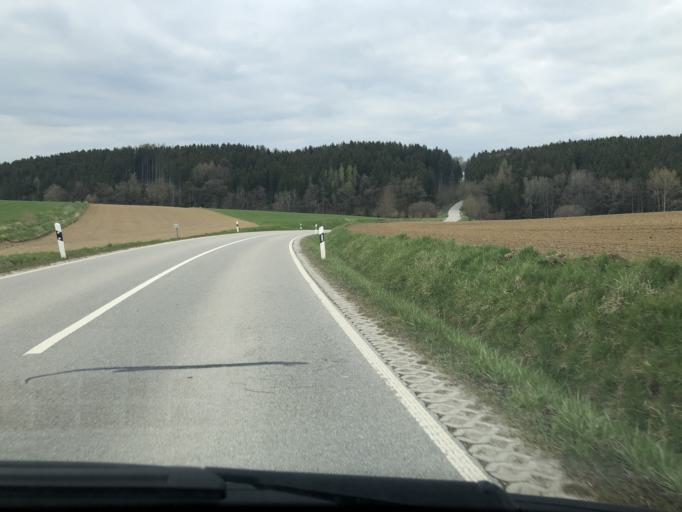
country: DE
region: Bavaria
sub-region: Upper Bavaria
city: Wolfersdorf
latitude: 48.4644
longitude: 11.7050
